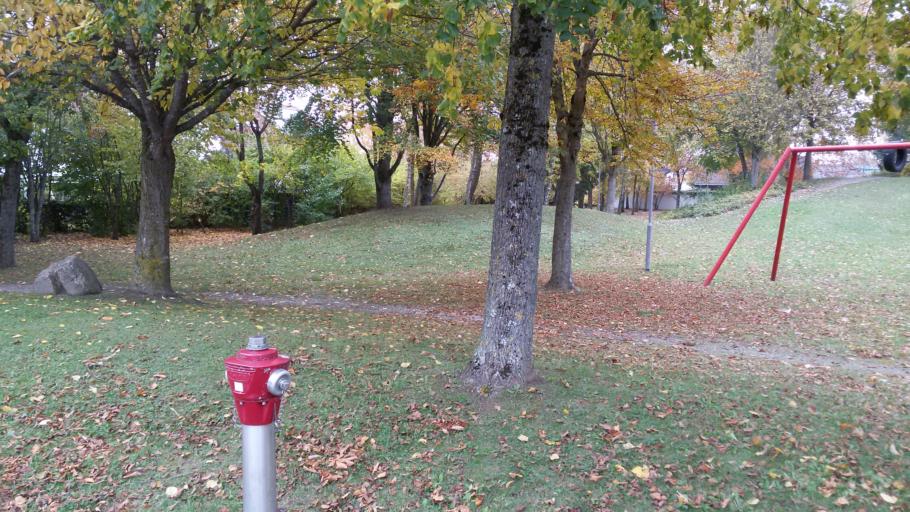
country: DE
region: Bavaria
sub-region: Swabia
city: Klosterlechfeld
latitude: 48.1539
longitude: 10.8286
